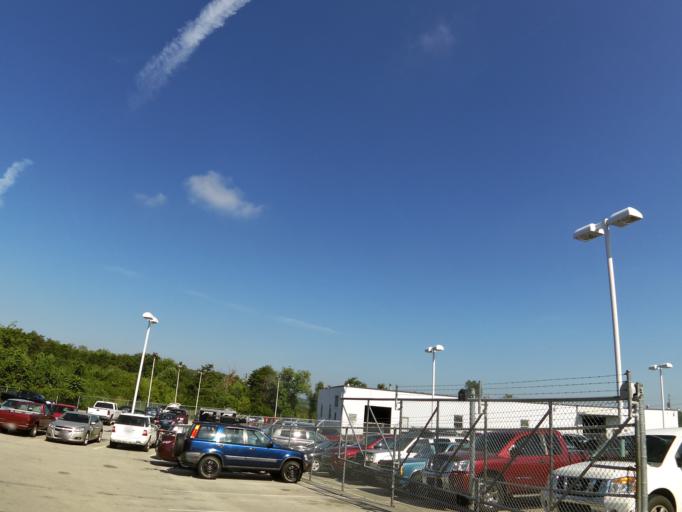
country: US
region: Tennessee
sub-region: Blount County
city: Alcoa
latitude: 35.8306
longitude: -83.9757
